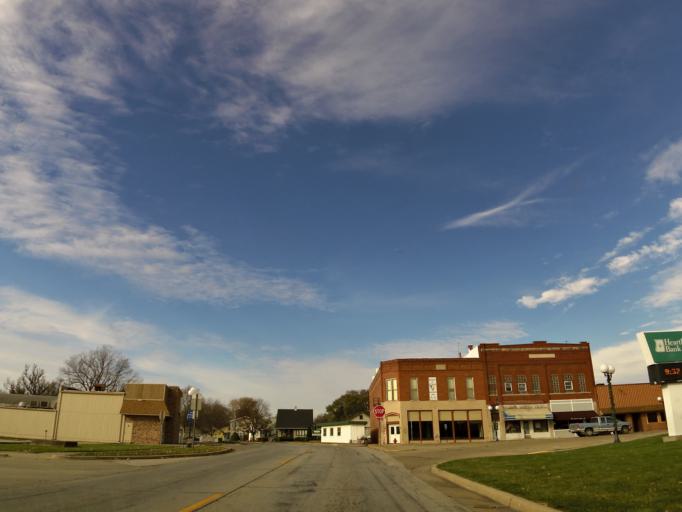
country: US
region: Illinois
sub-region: De Witt County
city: Farmer City
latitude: 40.2418
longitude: -88.6420
